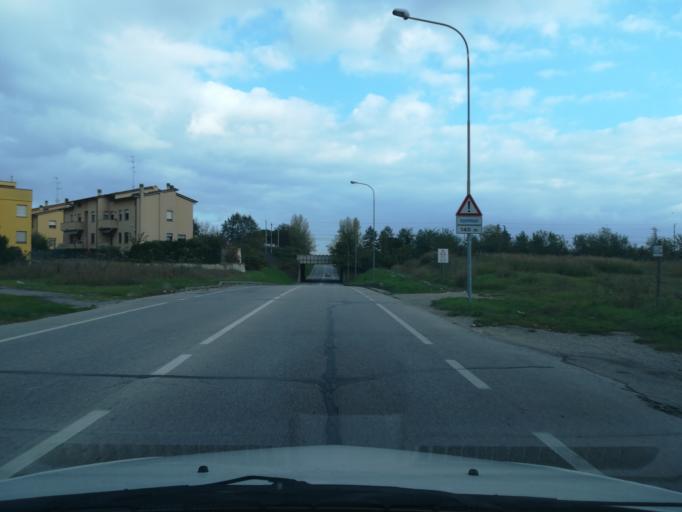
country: IT
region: Emilia-Romagna
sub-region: Provincia di Bologna
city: Imola
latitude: 44.3515
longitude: 11.7349
